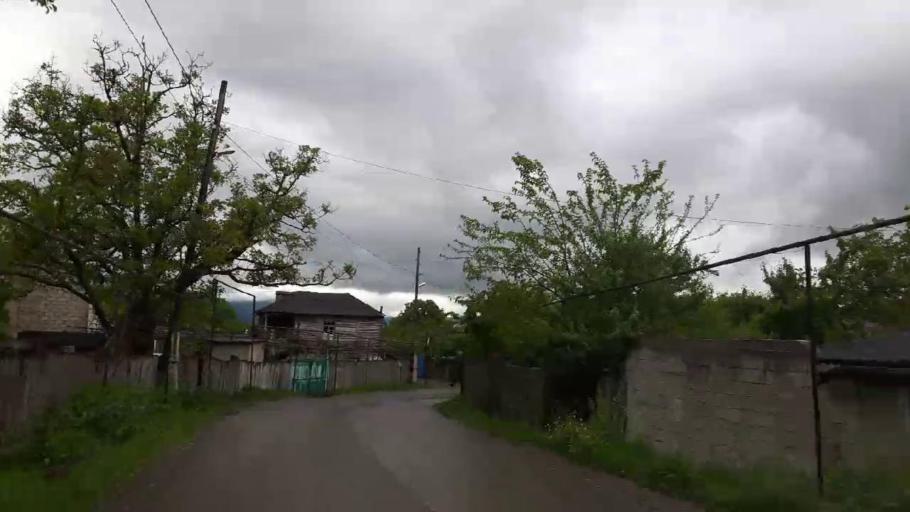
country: GE
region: Shida Kartli
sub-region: Khashuris Raioni
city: Khashuri
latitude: 41.9827
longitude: 43.6680
